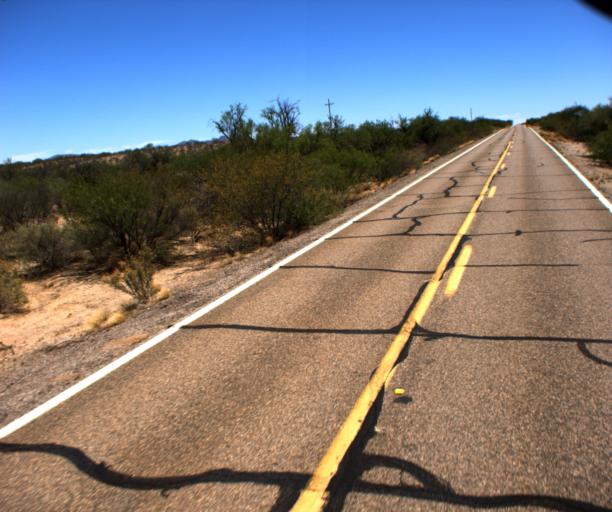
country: US
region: Arizona
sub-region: Pima County
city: Three Points
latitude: 31.9346
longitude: -111.3910
